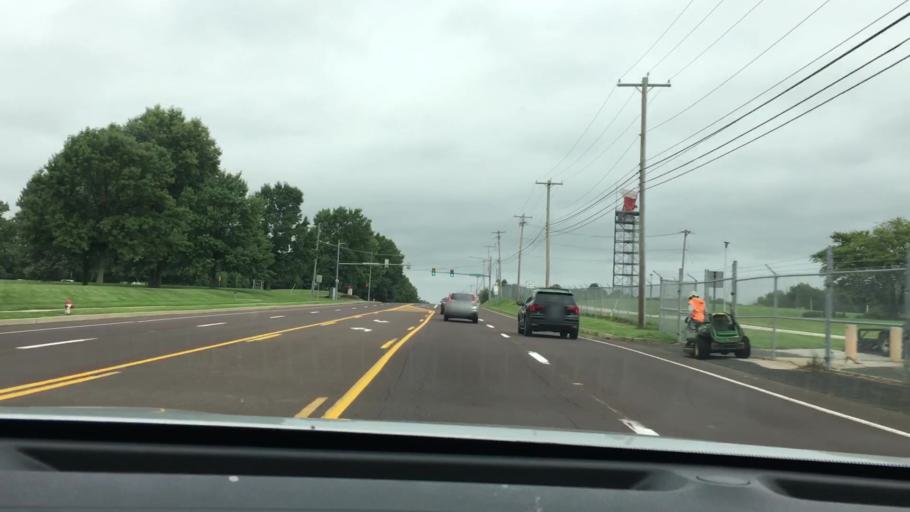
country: US
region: Pennsylvania
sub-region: Montgomery County
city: Horsham
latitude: 40.1918
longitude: -75.1516
